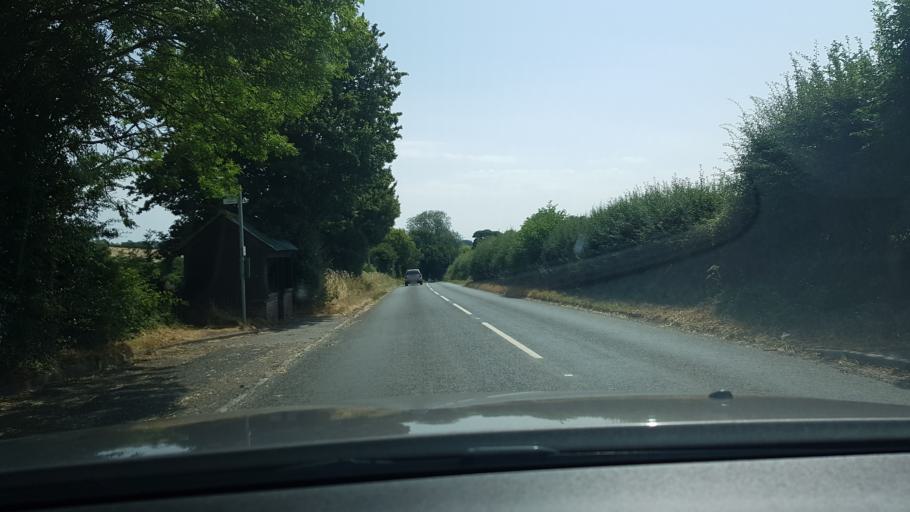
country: GB
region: England
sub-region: West Berkshire
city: Lambourn
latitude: 51.4875
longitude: -1.4784
